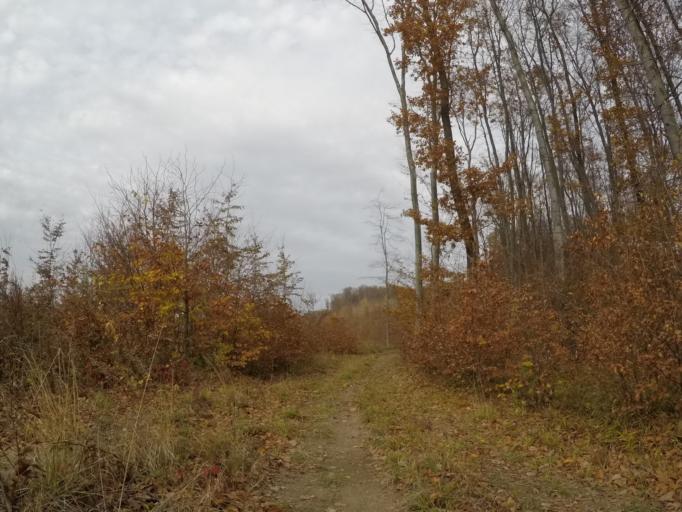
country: SK
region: Presovsky
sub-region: Okres Presov
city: Presov
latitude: 48.9590
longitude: 21.2118
